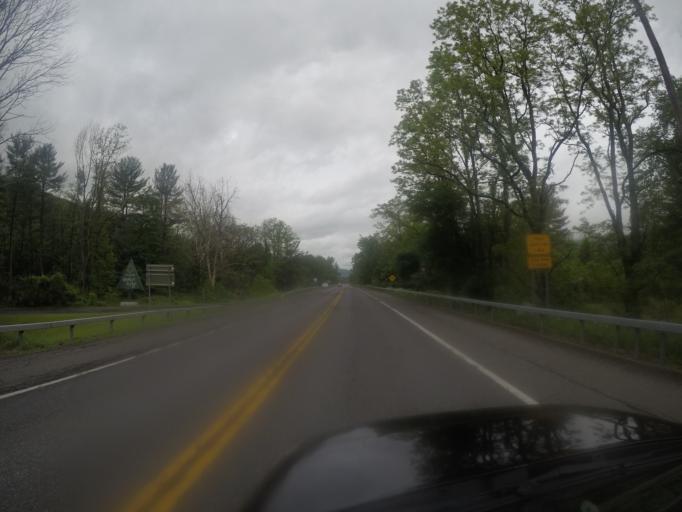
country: US
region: New York
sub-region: Ulster County
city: Shokan
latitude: 42.0399
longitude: -74.2793
